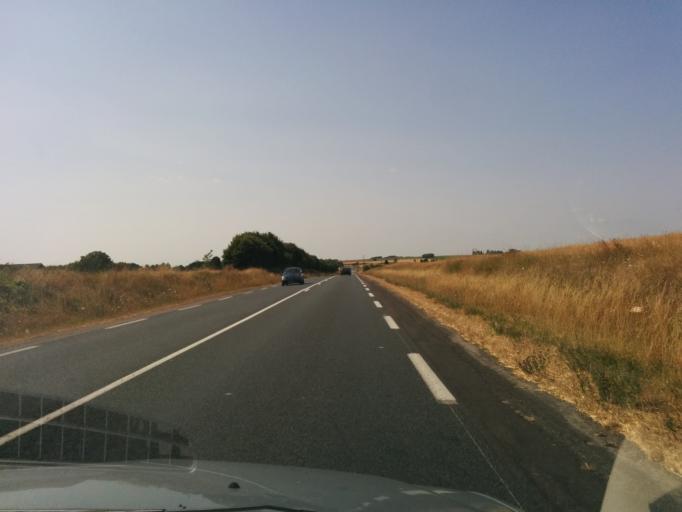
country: FR
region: Poitou-Charentes
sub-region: Departement de la Vienne
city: Neuville-de-Poitou
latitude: 46.7046
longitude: 0.2351
